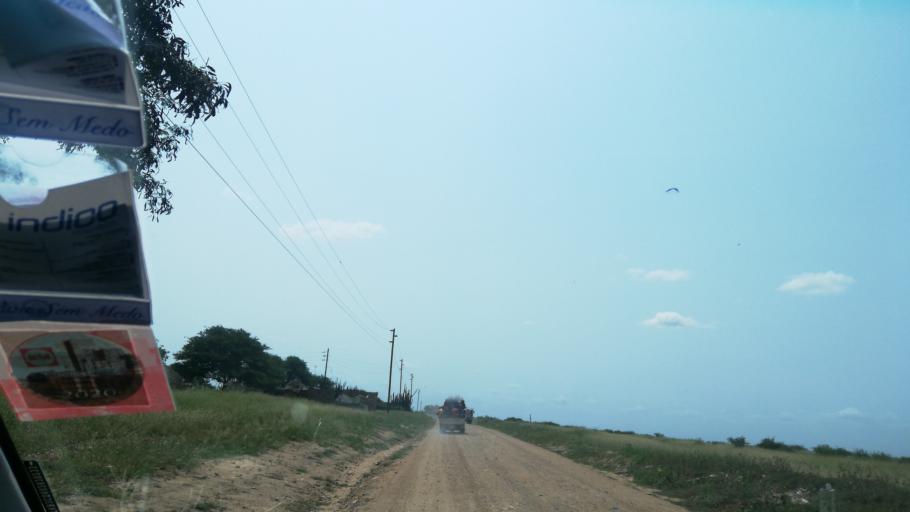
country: MZ
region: Maputo
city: Matola
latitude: -26.0650
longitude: 32.3903
